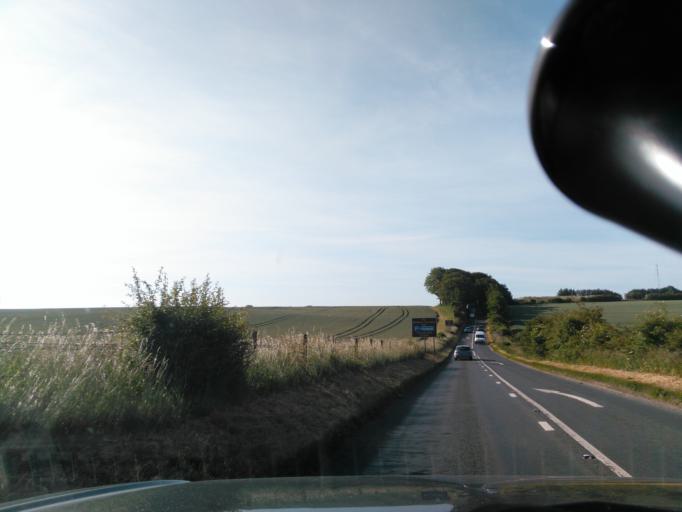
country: GB
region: England
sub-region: Wiltshire
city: Woodford
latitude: 51.1062
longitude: -1.8432
